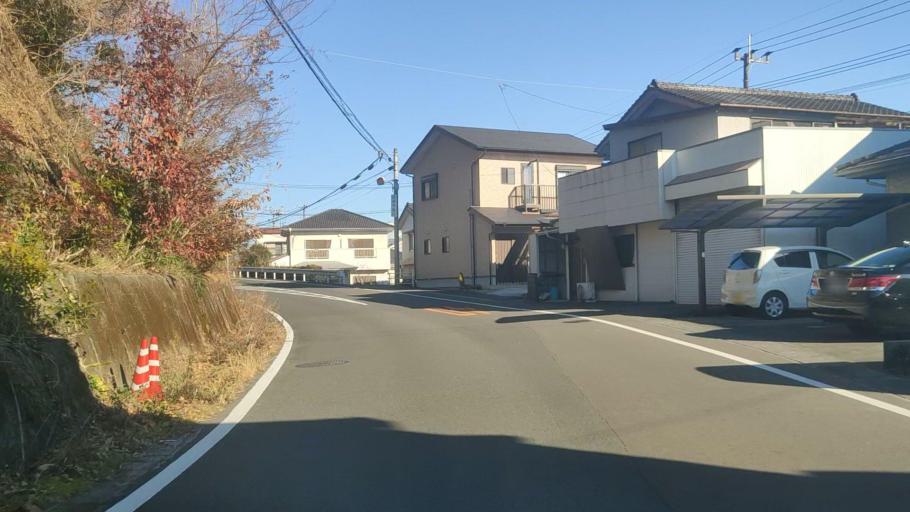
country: JP
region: Miyazaki
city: Nobeoka
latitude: 32.6108
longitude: 131.6889
